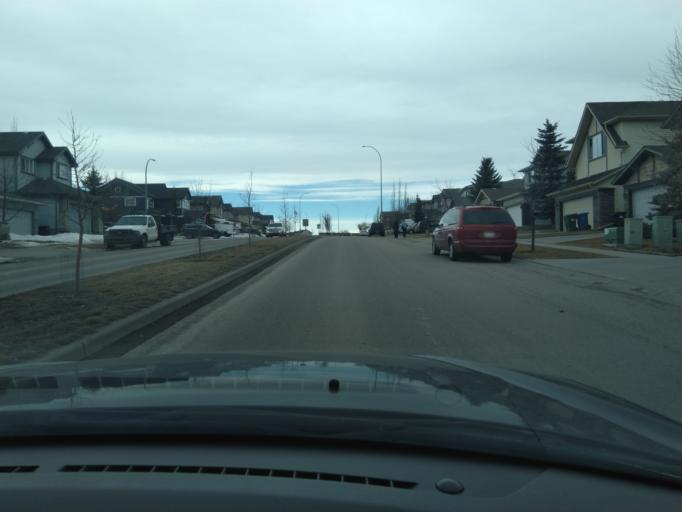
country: CA
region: Alberta
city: Calgary
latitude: 51.1633
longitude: -114.0839
